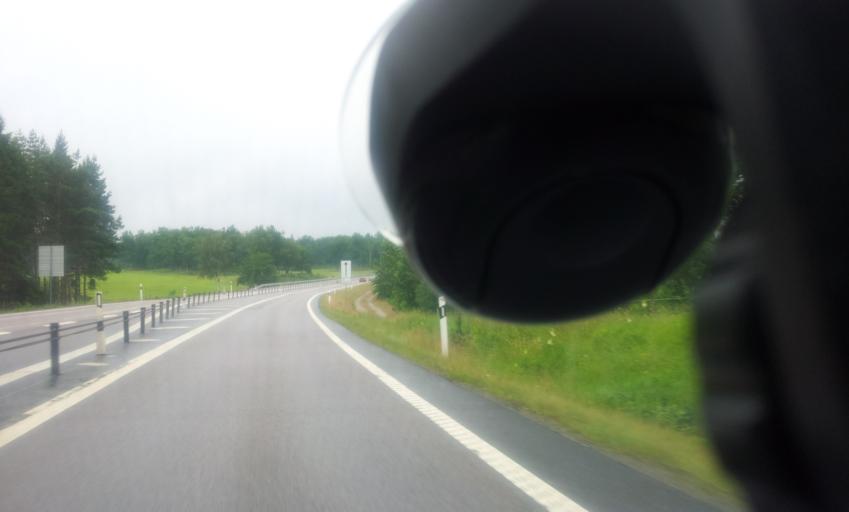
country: SE
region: Kalmar
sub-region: Vasterviks Kommun
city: Forserum
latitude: 58.0228
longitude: 16.5190
